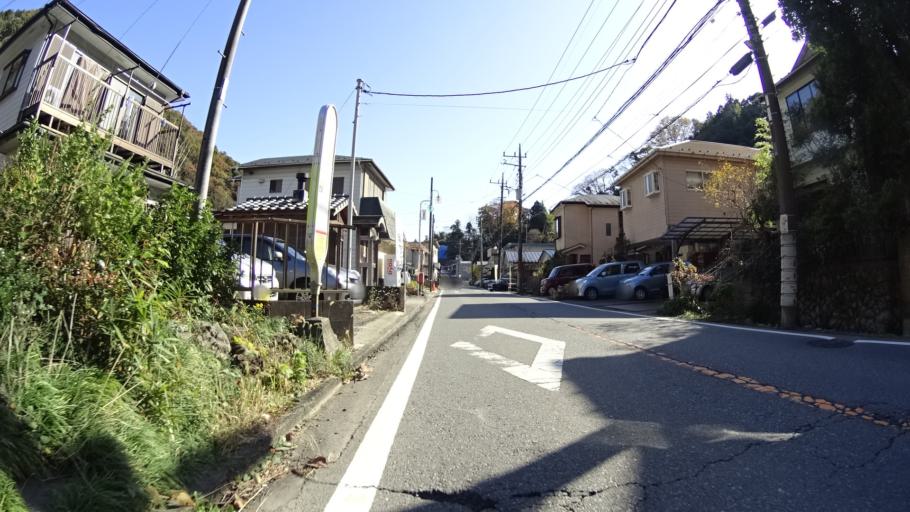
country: JP
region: Tokyo
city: Hachioji
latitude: 35.5416
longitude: 139.2763
